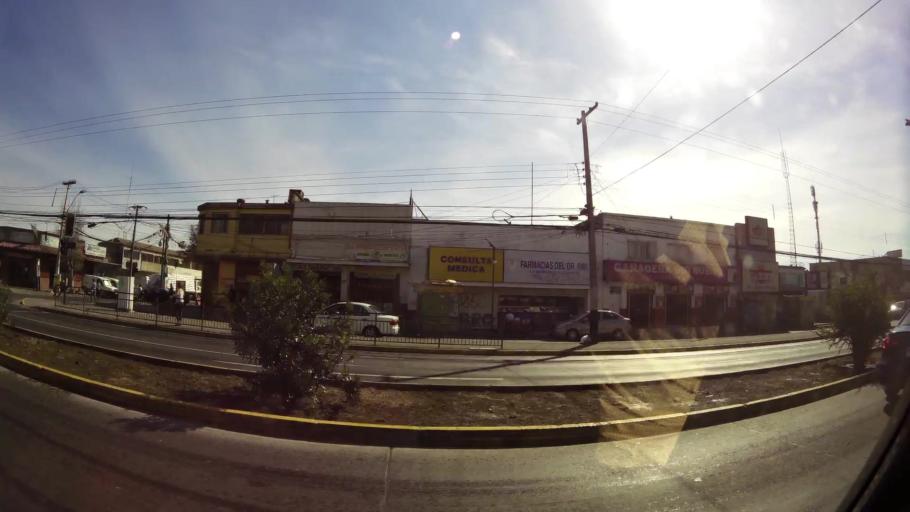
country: CL
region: Santiago Metropolitan
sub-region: Provincia de Santiago
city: La Pintana
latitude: -33.5340
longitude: -70.6347
